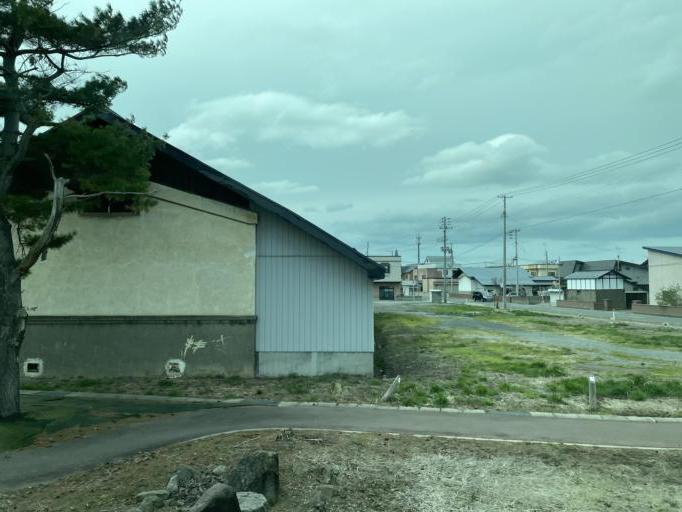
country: JP
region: Aomori
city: Goshogawara
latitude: 40.7586
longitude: 140.4355
